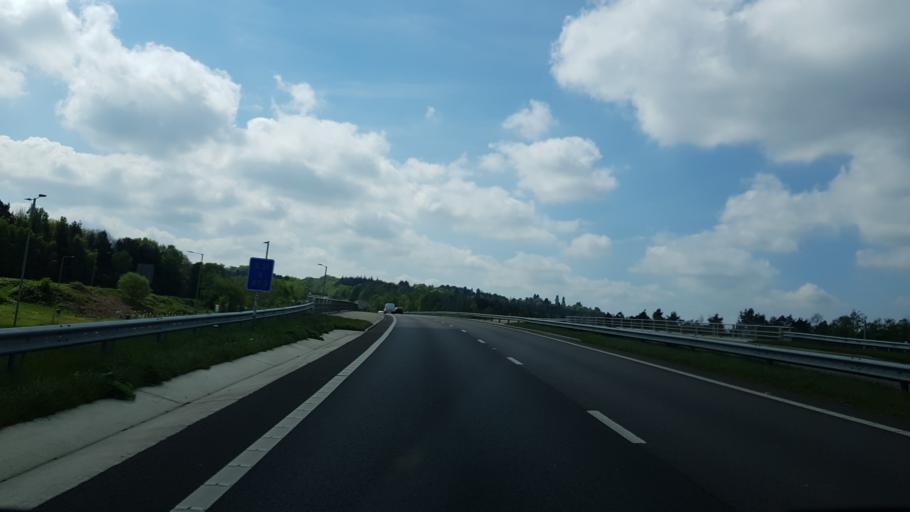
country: GB
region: England
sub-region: Kent
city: Pembury
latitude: 51.1572
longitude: 0.3039
